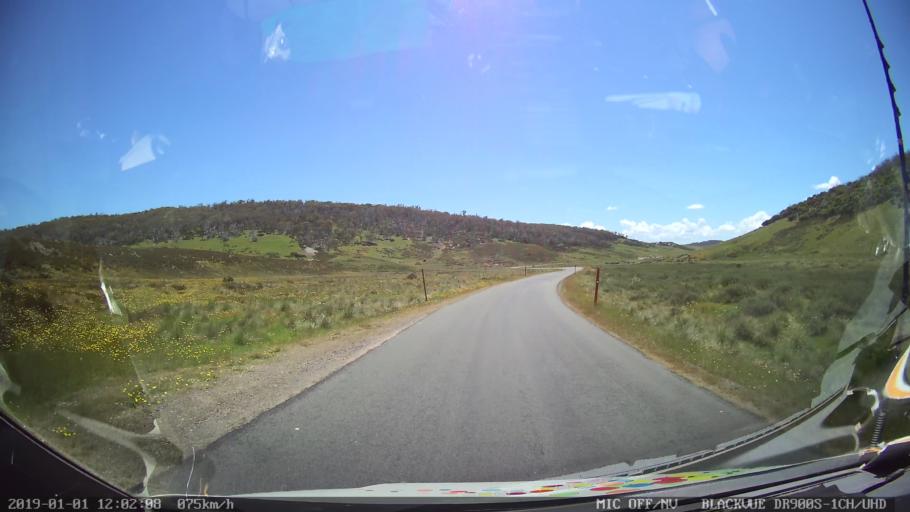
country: AU
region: New South Wales
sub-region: Snowy River
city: Jindabyne
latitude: -35.8745
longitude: 148.4740
